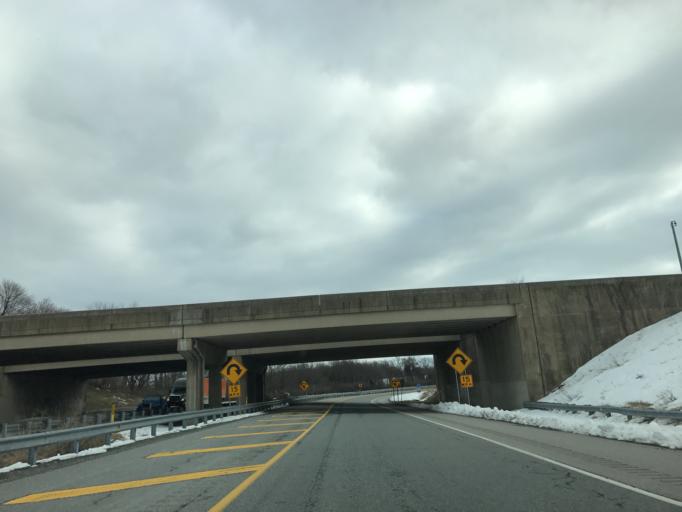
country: US
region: Pennsylvania
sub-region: York County
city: Shiloh
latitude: 39.9376
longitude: -76.7990
